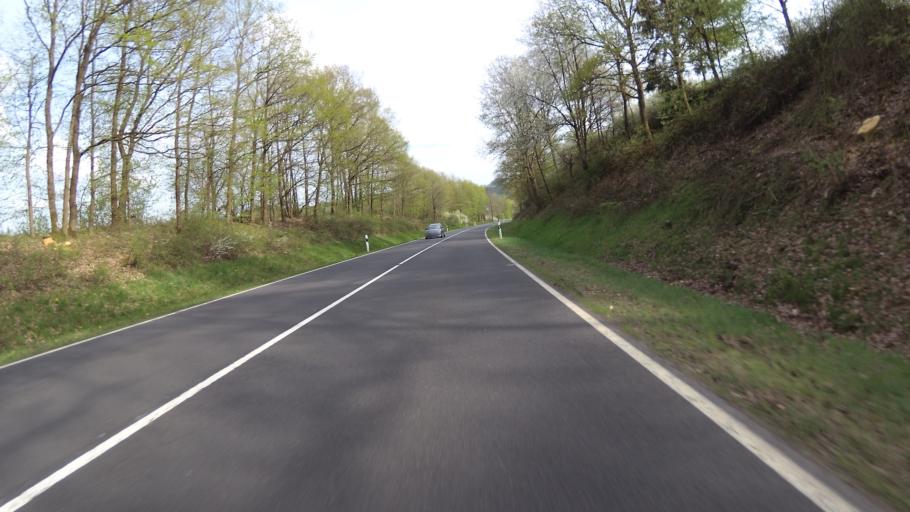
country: DE
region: Rheinland-Pfalz
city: Berenbach
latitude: 50.2274
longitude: 6.9510
